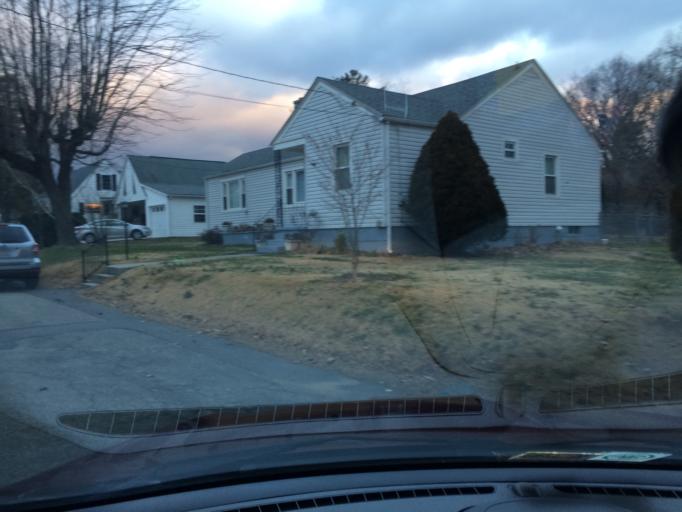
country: US
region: Virginia
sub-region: Alleghany County
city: Clifton Forge
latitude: 37.8234
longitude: -79.8171
